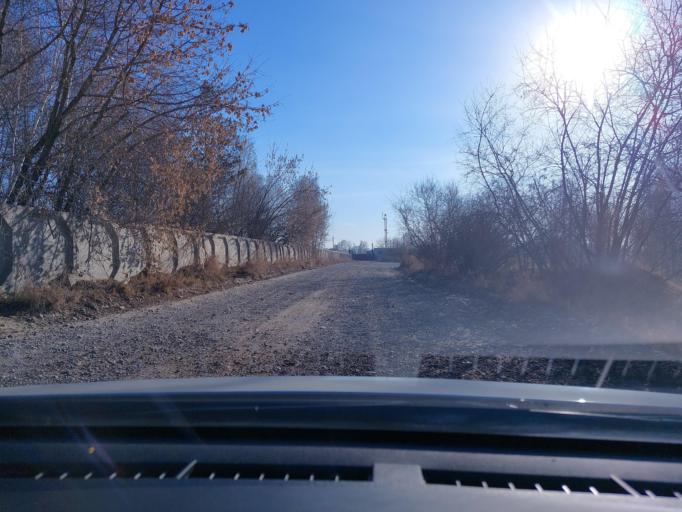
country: RU
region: Irkutsk
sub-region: Irkutskiy Rayon
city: Irkutsk
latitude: 52.3094
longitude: 104.2720
